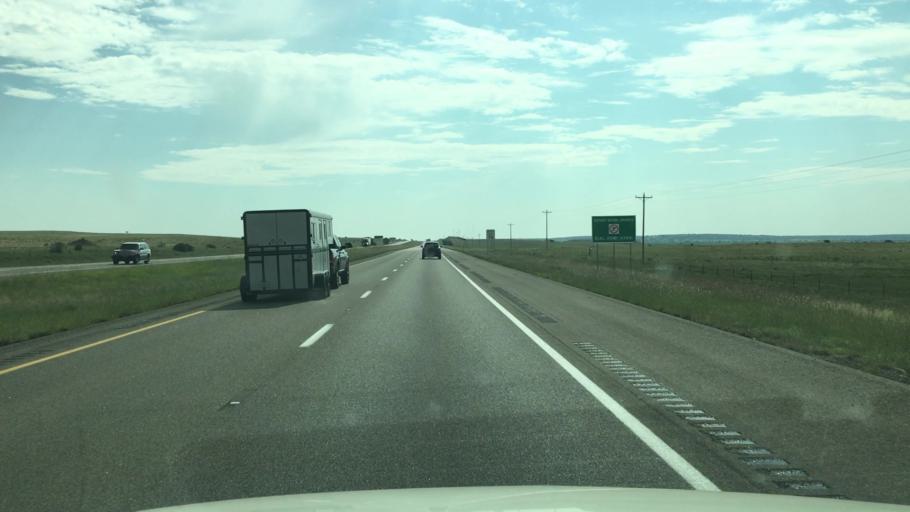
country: US
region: New Mexico
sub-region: Guadalupe County
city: Santa Rosa
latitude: 34.9909
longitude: -105.2861
